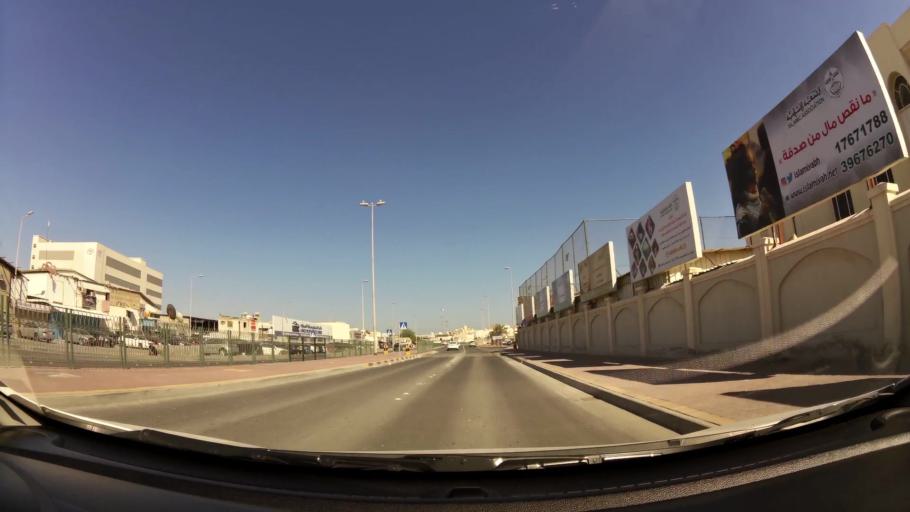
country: BH
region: Muharraq
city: Al Hadd
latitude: 26.2563
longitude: 50.6435
